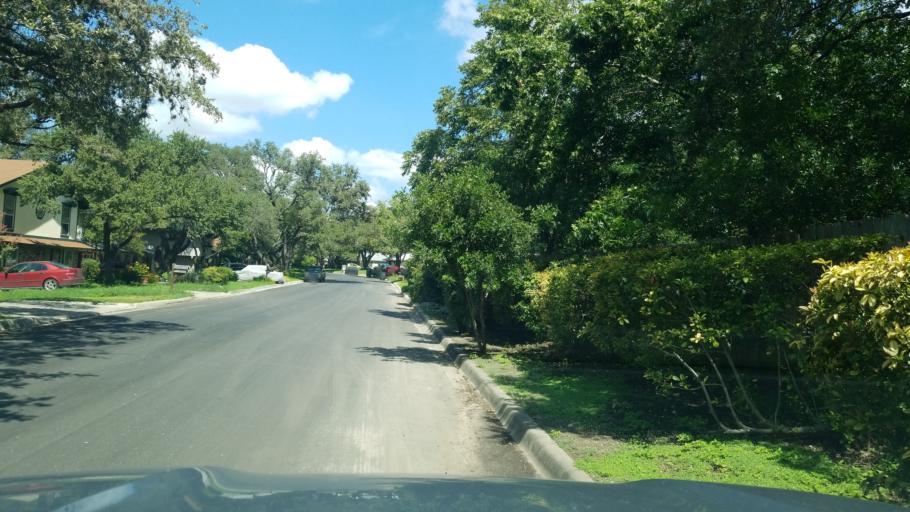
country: US
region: Texas
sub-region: Bexar County
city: Castle Hills
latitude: 29.5462
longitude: -98.4995
